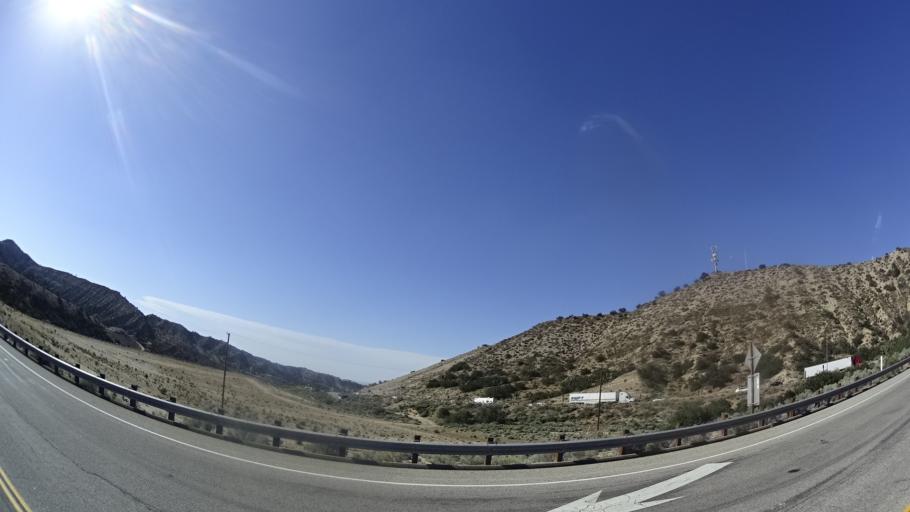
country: US
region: California
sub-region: San Bernardino County
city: Phelan
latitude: 34.3904
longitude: -117.5779
